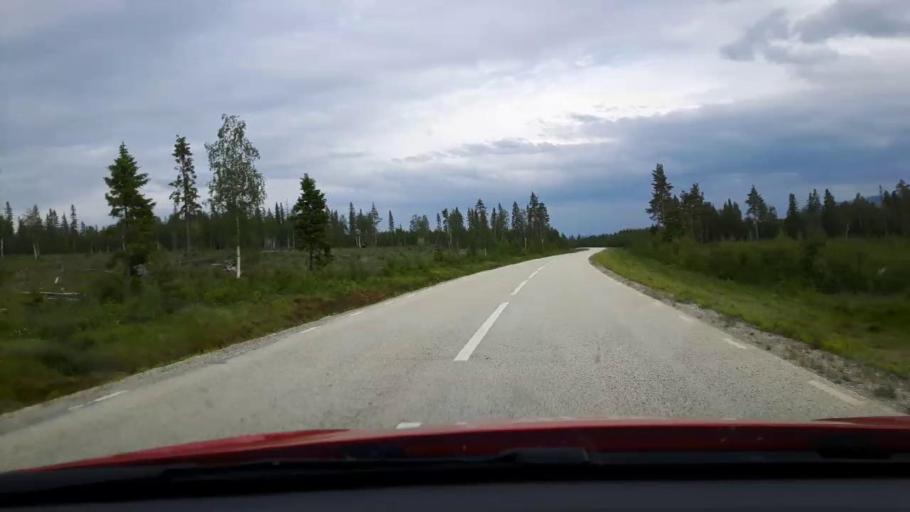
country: SE
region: Jaemtland
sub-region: Bergs Kommun
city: Hoverberg
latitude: 62.7015
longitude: 13.9550
